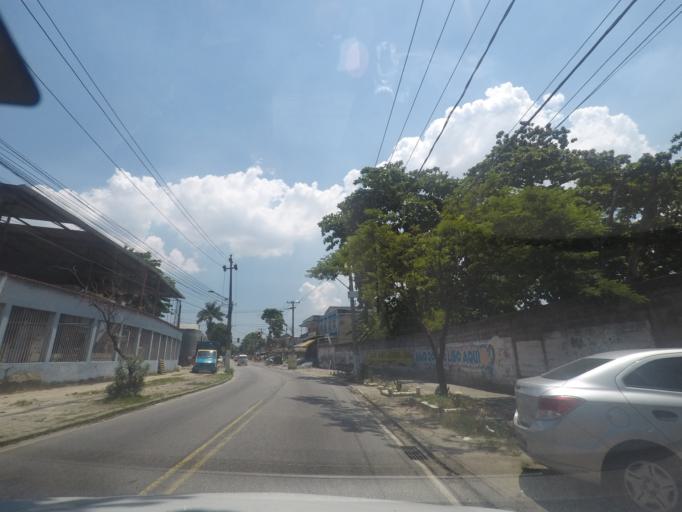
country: BR
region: Rio de Janeiro
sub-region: Duque De Caxias
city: Duque de Caxias
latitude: -22.8206
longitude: -43.3063
